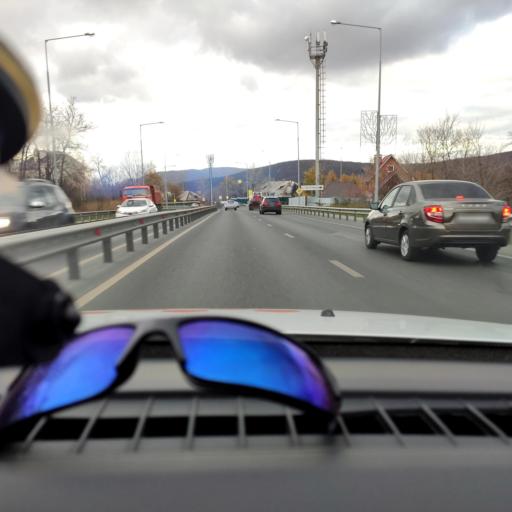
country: RU
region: Samara
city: Volzhskiy
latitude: 53.3635
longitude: 50.2020
